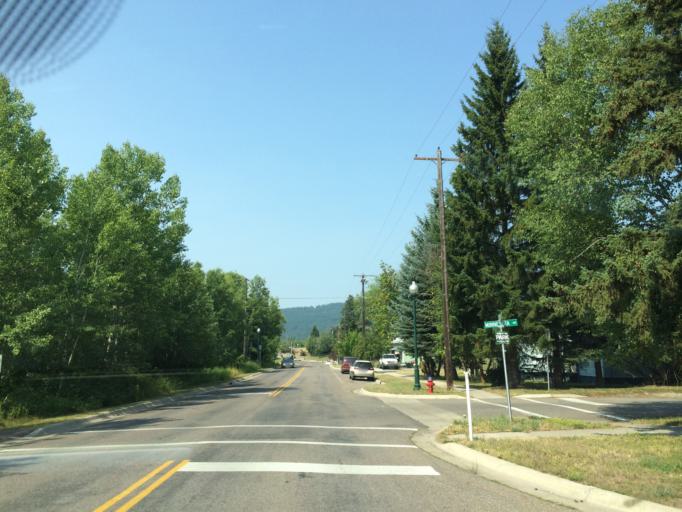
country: US
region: Montana
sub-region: Flathead County
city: Whitefish
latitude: 48.4152
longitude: -114.3448
